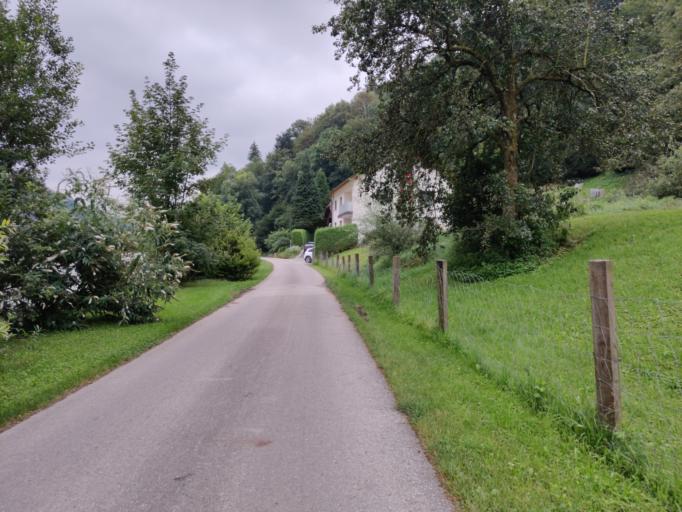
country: AT
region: Lower Austria
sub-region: Politischer Bezirk Melk
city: Nochling
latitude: 48.2196
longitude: 14.9475
